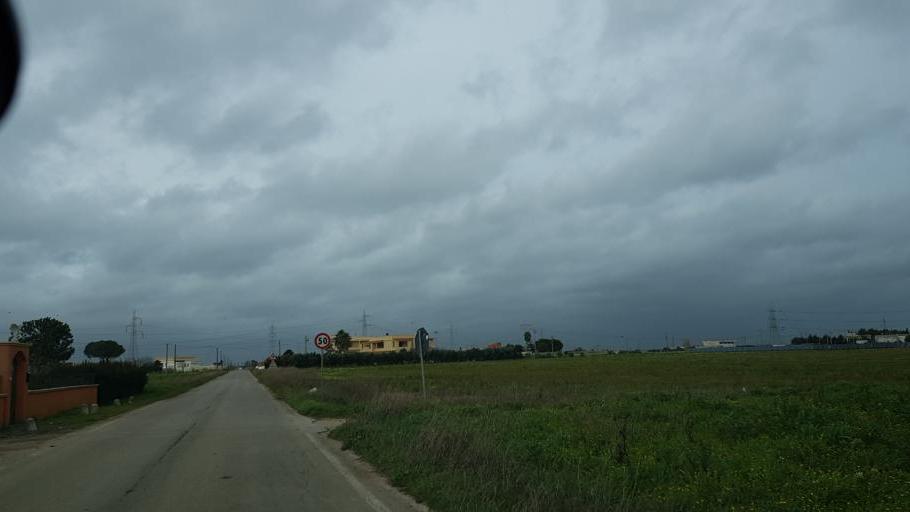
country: IT
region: Apulia
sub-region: Provincia di Brindisi
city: La Rosa
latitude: 40.5924
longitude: 17.9132
